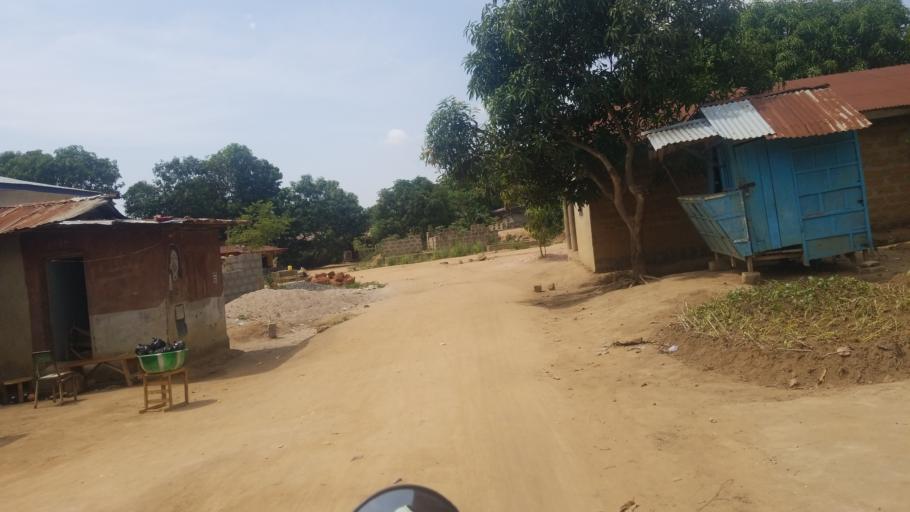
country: SL
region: Western Area
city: Waterloo
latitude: 8.3156
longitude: -13.0482
